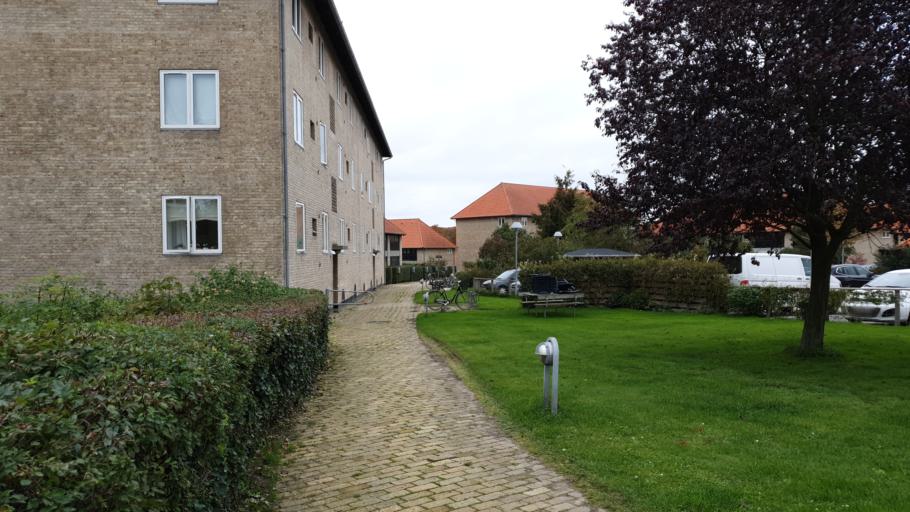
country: DK
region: Capital Region
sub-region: Rudersdal Kommune
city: Trorod
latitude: 55.8110
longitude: 12.5369
